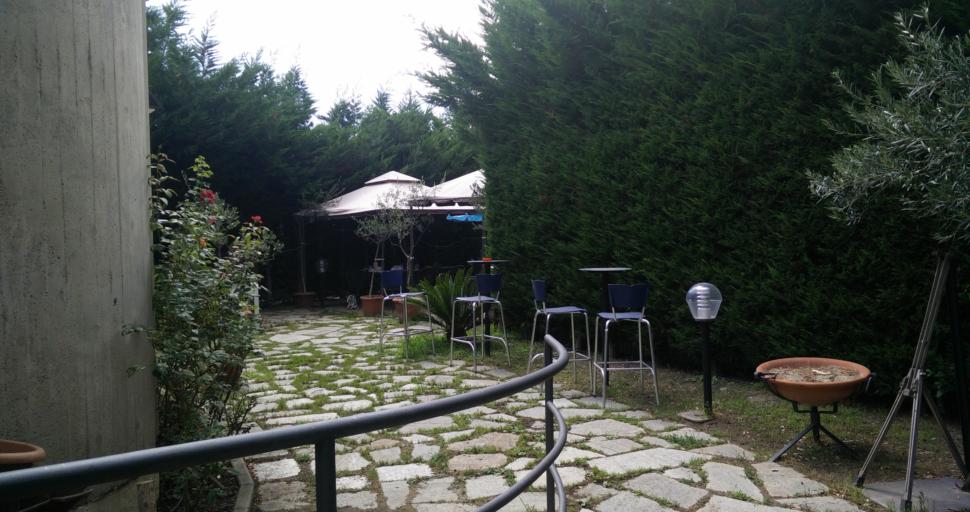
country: IT
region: Liguria
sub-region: Provincia di Imperia
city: Taggia
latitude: 43.8525
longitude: 7.8575
